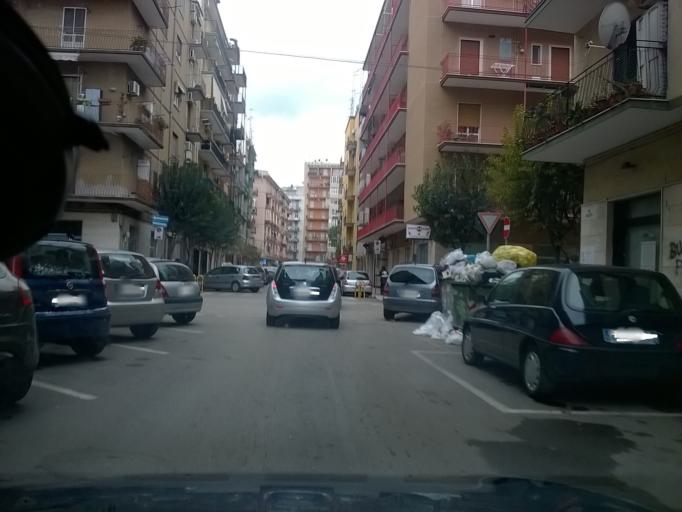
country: IT
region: Apulia
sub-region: Provincia di Taranto
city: Taranto
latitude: 40.4594
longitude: 17.2614
